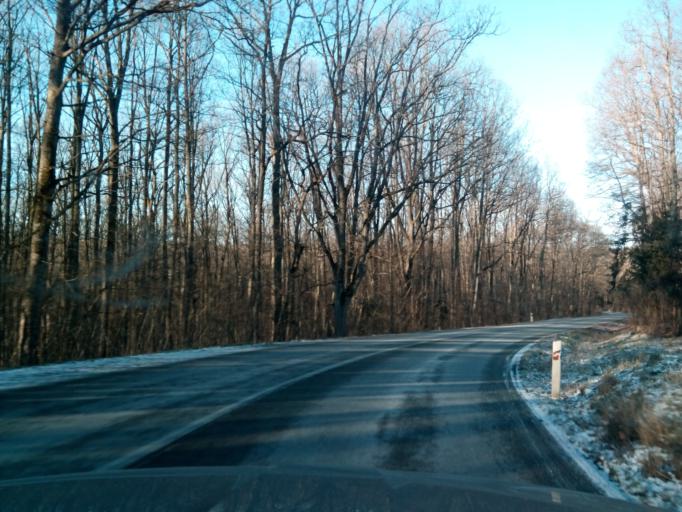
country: SK
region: Kosicky
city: Moldava nad Bodvou
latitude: 48.6872
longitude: 21.0401
